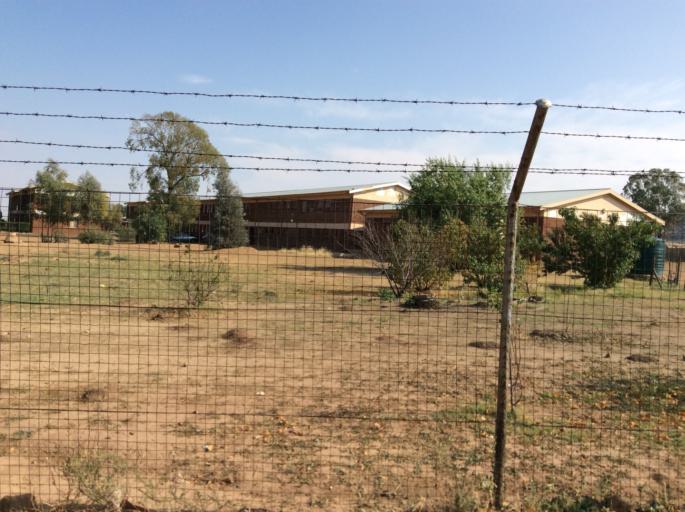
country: LS
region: Mafeteng
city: Mafeteng
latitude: -29.7169
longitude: 27.0322
